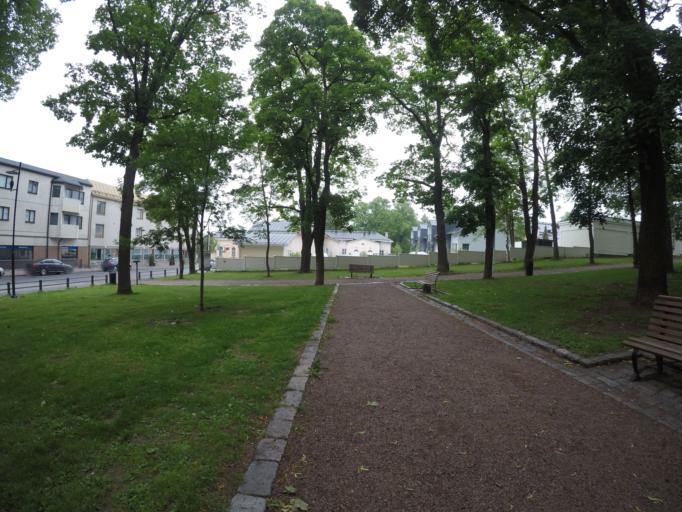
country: FI
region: Haeme
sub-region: Haemeenlinna
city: Haemeenlinna
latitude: 60.9980
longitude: 24.4631
